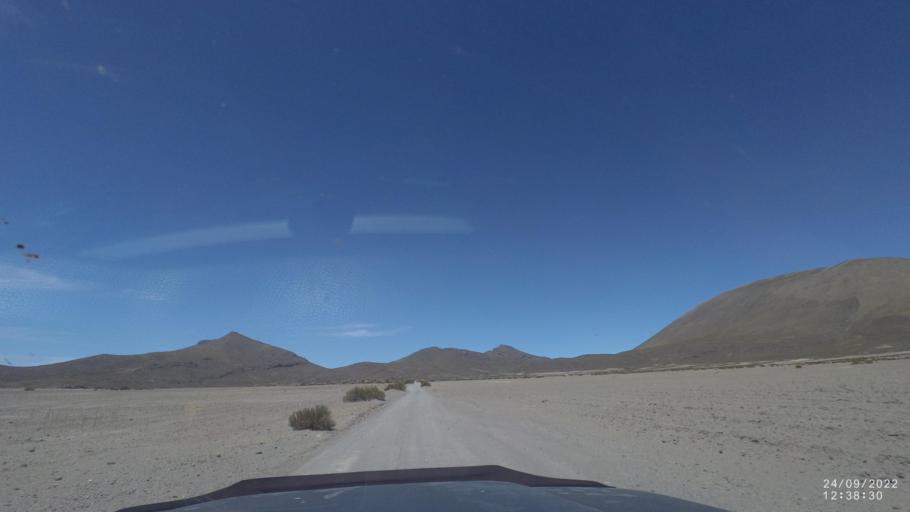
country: BO
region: Potosi
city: Colchani
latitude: -19.7899
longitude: -67.5847
